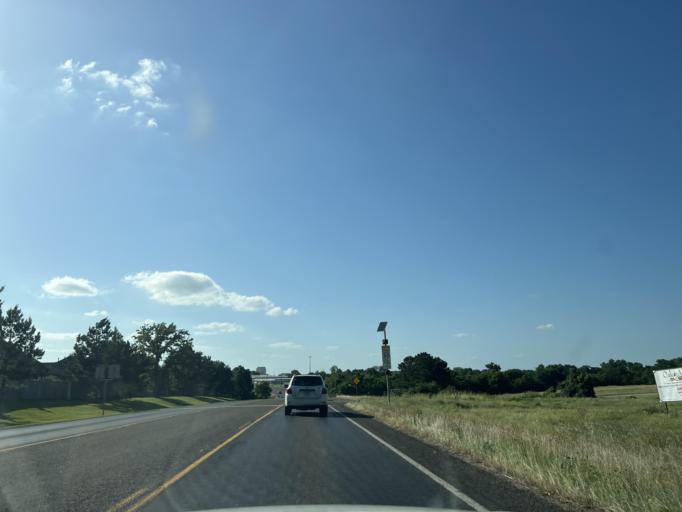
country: US
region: Texas
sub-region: Washington County
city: Brenham
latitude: 30.1527
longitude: -96.3681
